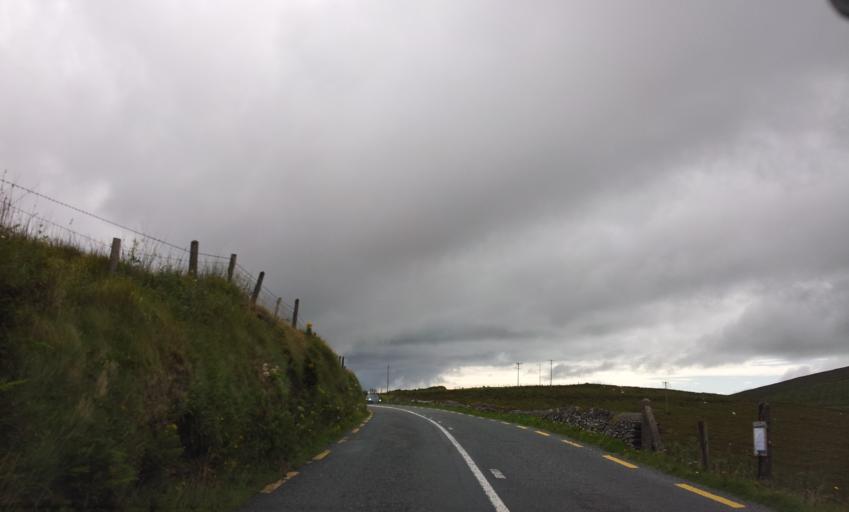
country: IE
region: Munster
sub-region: Ciarrai
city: Killorglin
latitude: 52.1990
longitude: -9.9300
